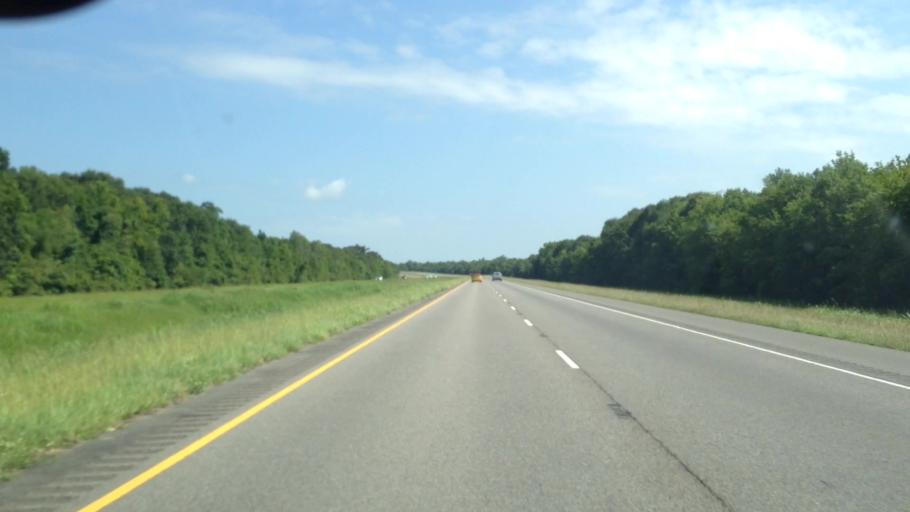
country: US
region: Louisiana
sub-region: Avoyelles Parish
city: Bunkie
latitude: 30.8882
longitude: -92.2269
